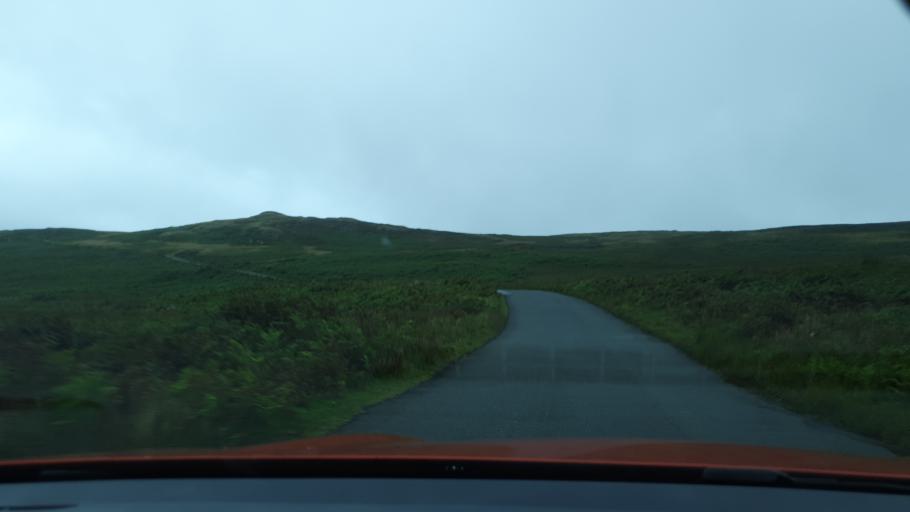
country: GB
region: England
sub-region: Cumbria
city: Millom
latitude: 54.3738
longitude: -3.2842
